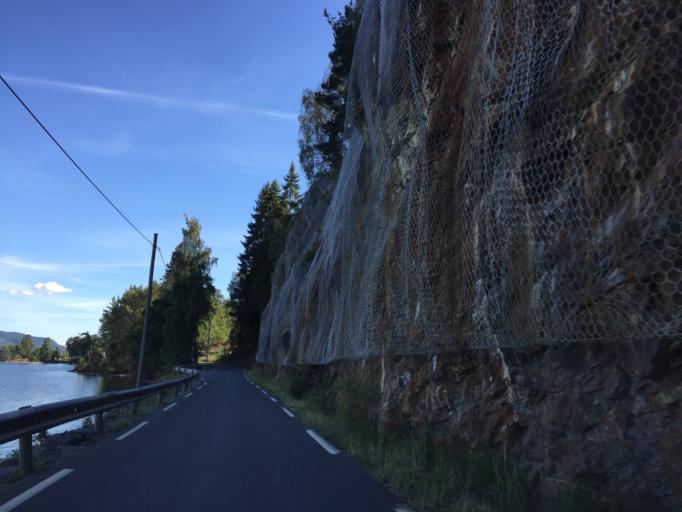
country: NO
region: Buskerud
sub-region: Ovre Eiker
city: Hokksund
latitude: 59.6788
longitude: 9.8627
